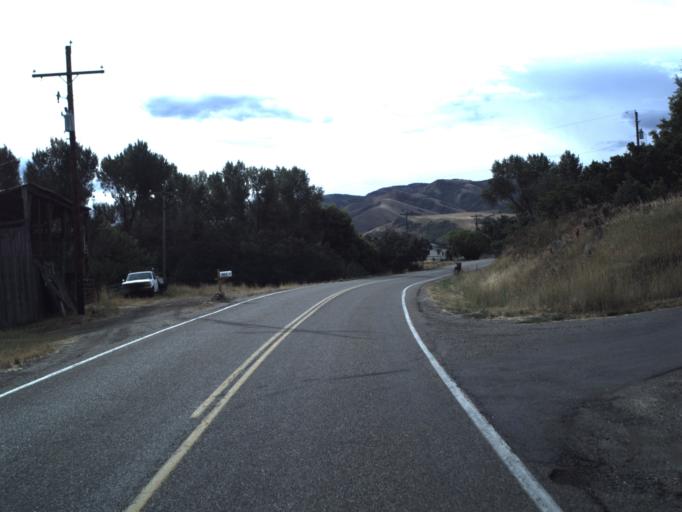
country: US
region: Utah
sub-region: Morgan County
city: Morgan
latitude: 40.9617
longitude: -111.6689
